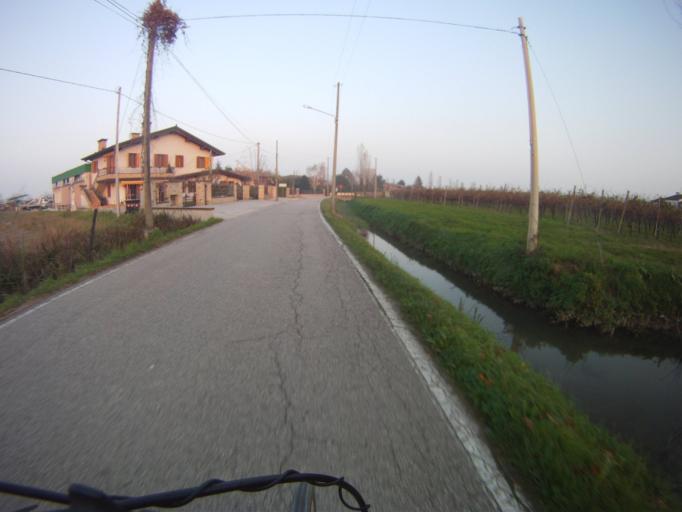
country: IT
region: Veneto
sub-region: Provincia di Padova
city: Albignasego
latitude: 45.3592
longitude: 11.9013
